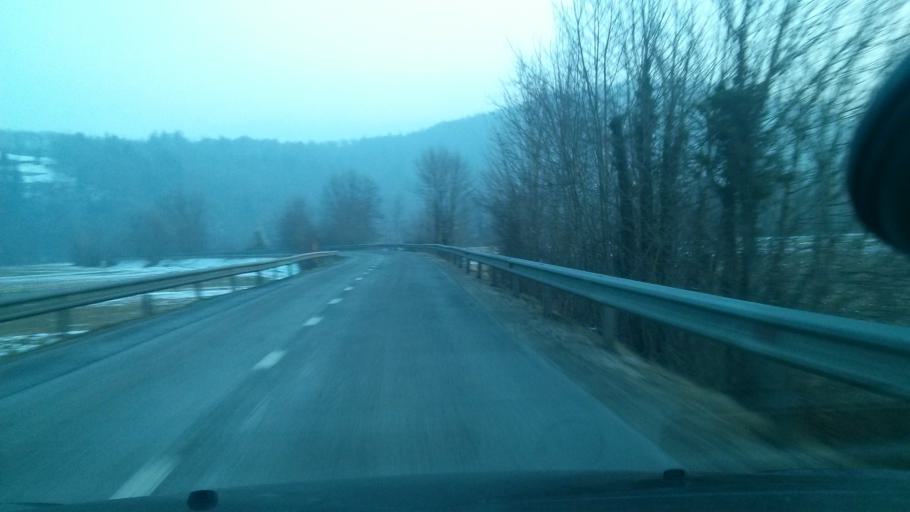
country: SI
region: Litija
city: Litija
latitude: 46.0907
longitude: 14.8331
